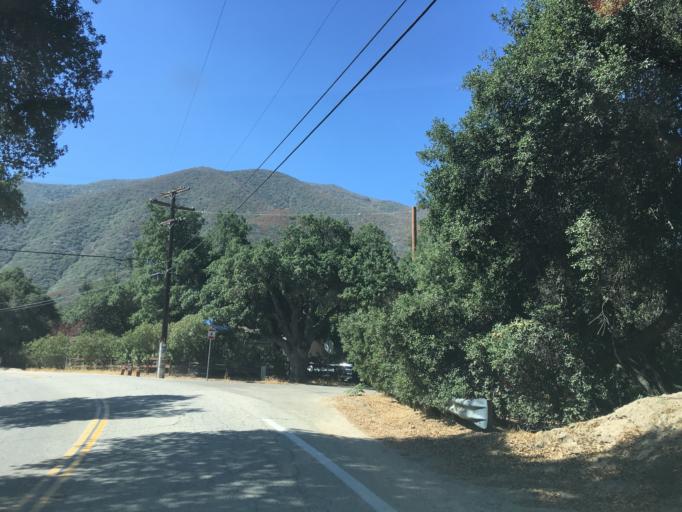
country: US
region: California
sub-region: Los Angeles County
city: Green Valley
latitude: 34.6199
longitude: -118.4138
